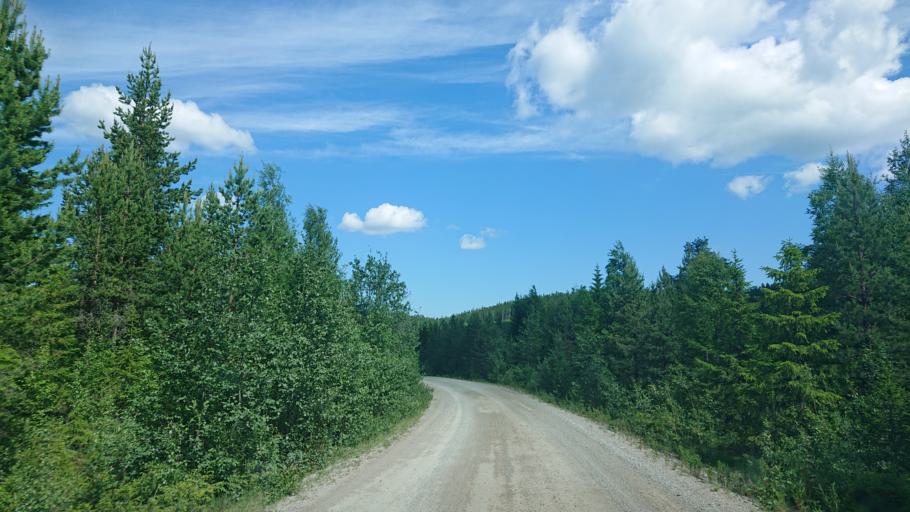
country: SE
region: Vaesternorrland
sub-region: Solleftea Kommun
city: Solleftea
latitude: 62.9342
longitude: 17.1251
